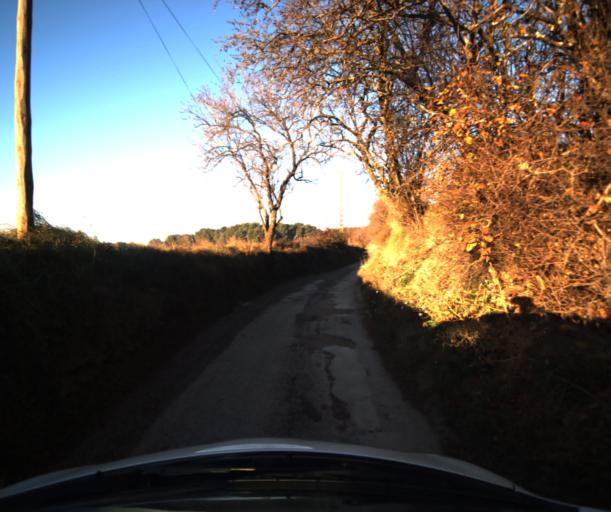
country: FR
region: Provence-Alpes-Cote d'Azur
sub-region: Departement du Vaucluse
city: Pertuis
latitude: 43.7044
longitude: 5.4880
